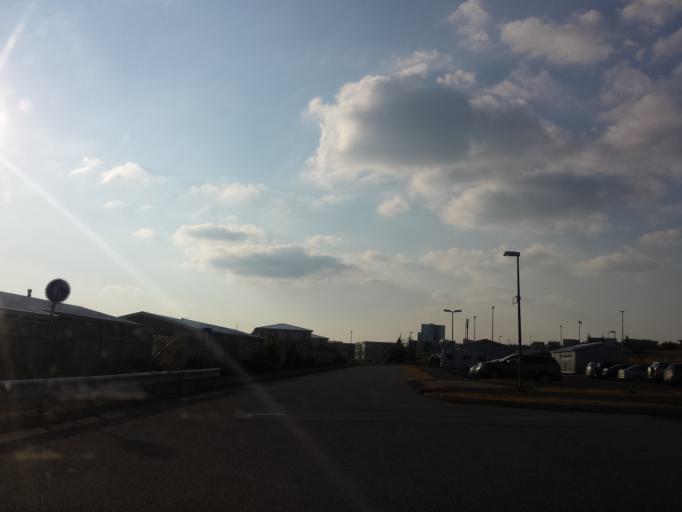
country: IS
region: Capital Region
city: Reykjavik
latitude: 64.0887
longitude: -21.8035
